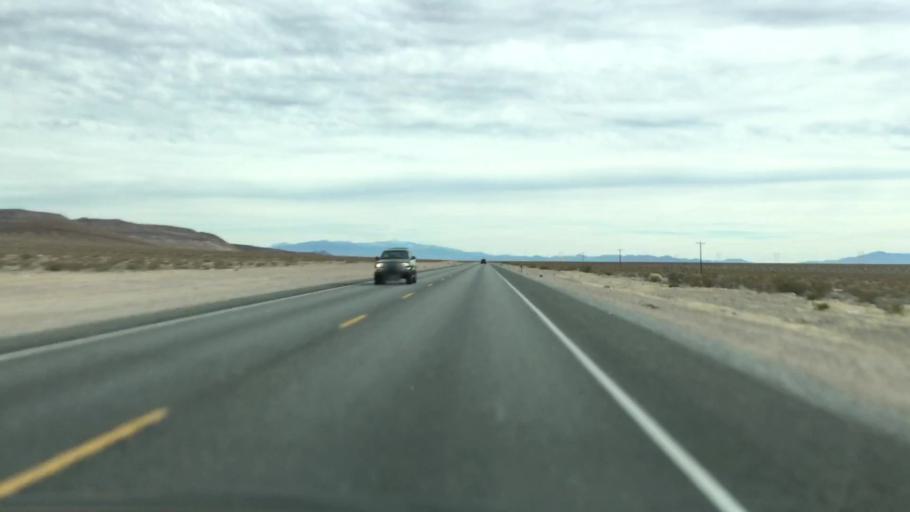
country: US
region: Nevada
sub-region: Nye County
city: Beatty
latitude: 36.7007
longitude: -116.5824
